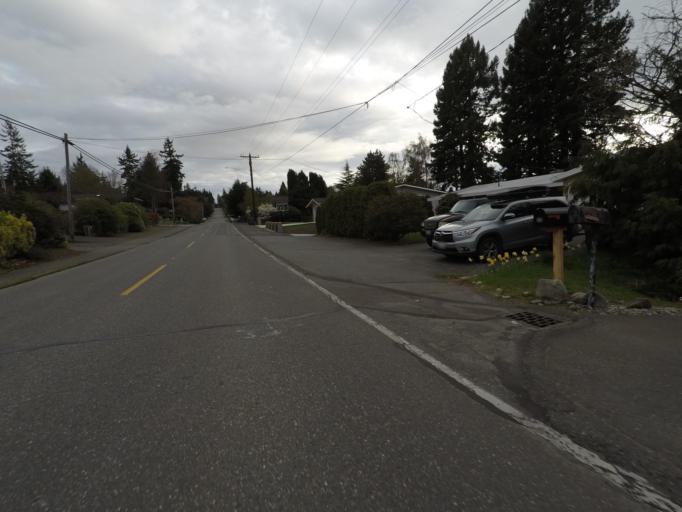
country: US
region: Washington
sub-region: Snohomish County
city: Edmonds
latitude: 47.8164
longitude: -122.3617
